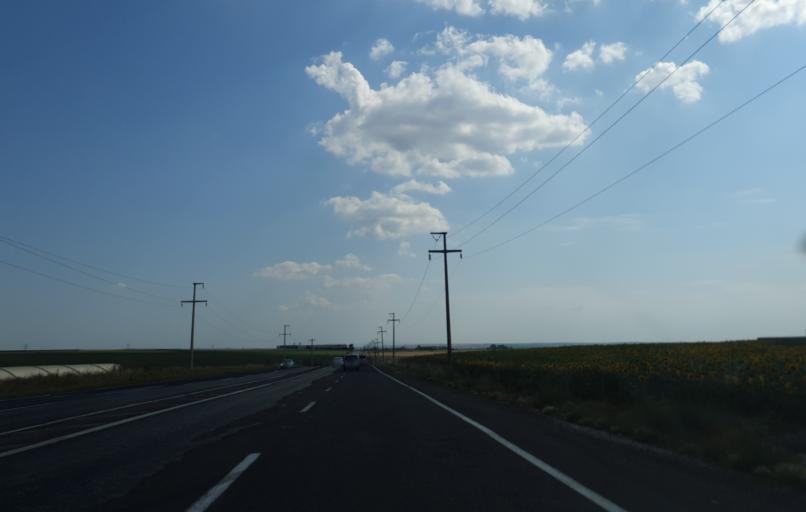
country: TR
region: Kirklareli
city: Buyukkaristiran
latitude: 41.2667
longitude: 27.5499
